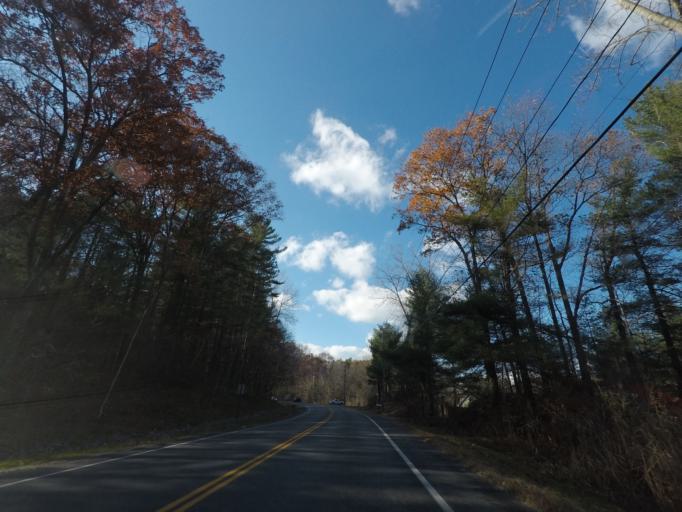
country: US
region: New York
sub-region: Saratoga County
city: Country Knolls
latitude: 42.8887
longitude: -73.8053
